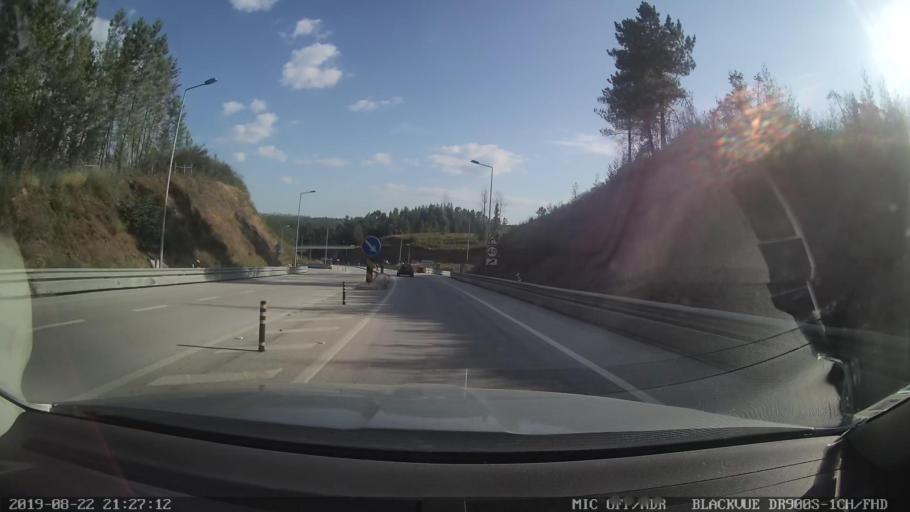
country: PT
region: Leiria
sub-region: Pedrogao Grande
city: Pedrogao Grande
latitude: 39.8746
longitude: -8.1180
